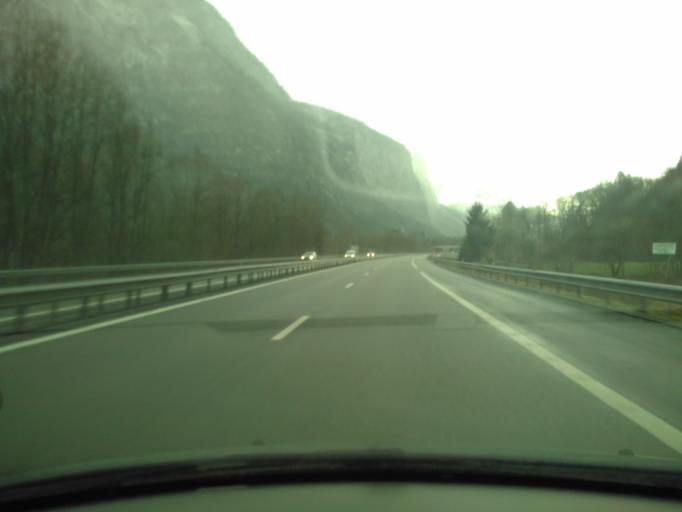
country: FR
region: Rhone-Alpes
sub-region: Departement de la Haute-Savoie
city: Magland
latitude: 46.0358
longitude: 6.6106
